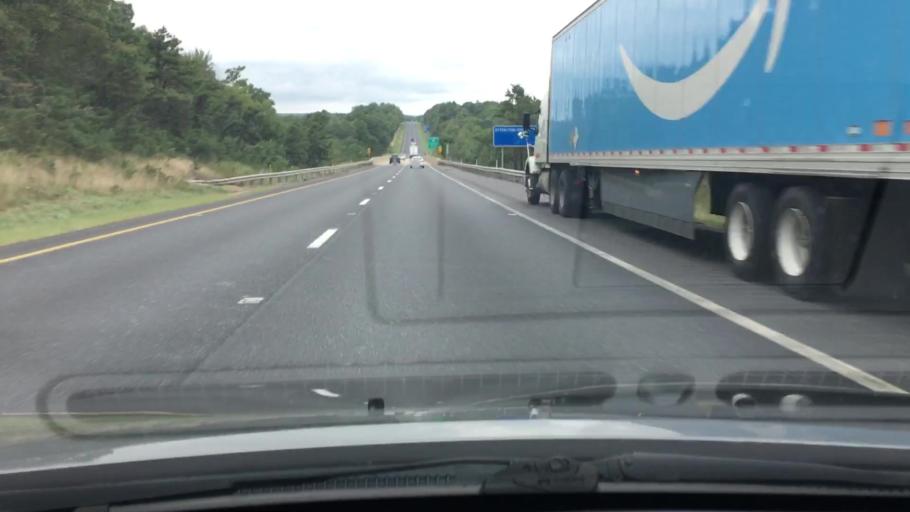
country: US
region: Pennsylvania
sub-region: Schuylkill County
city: Shenandoah
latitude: 40.7800
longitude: -76.1800
